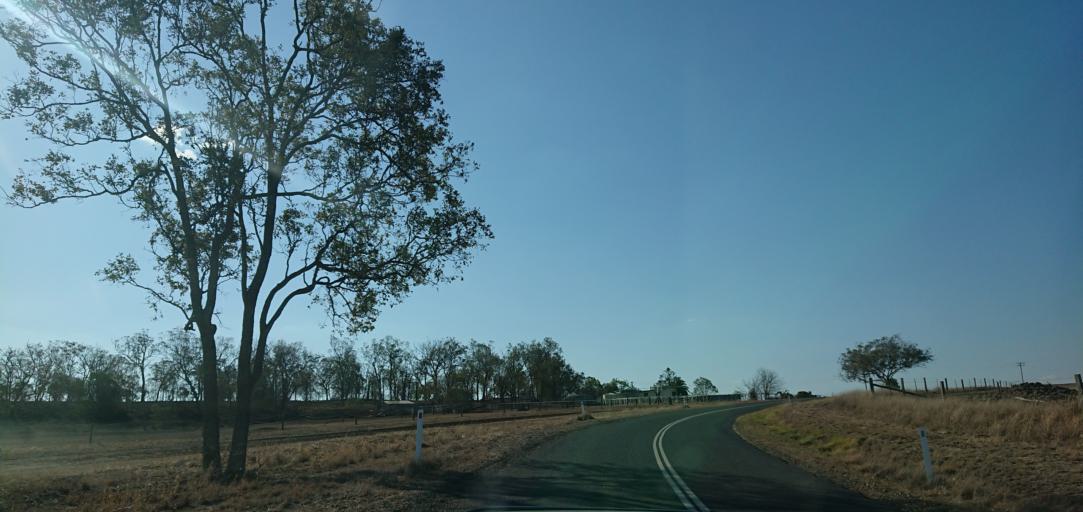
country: AU
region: Queensland
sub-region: Toowoomba
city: Westbrook
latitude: -27.7189
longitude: 151.7198
